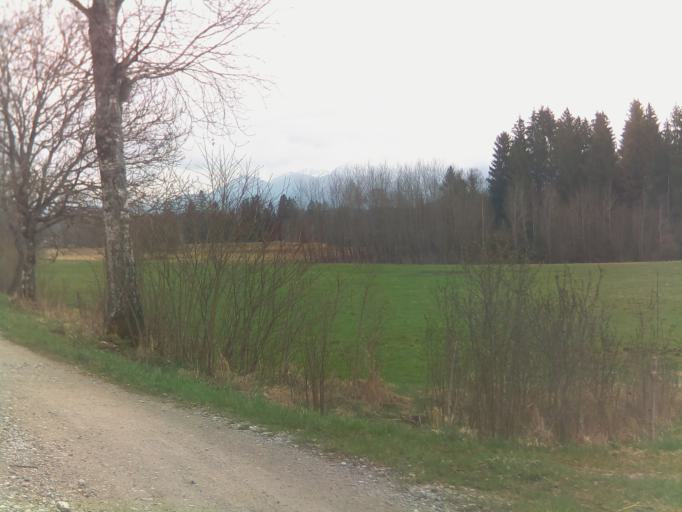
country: DE
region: Bavaria
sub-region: Upper Bavaria
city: Uffing
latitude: 47.6925
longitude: 11.1165
